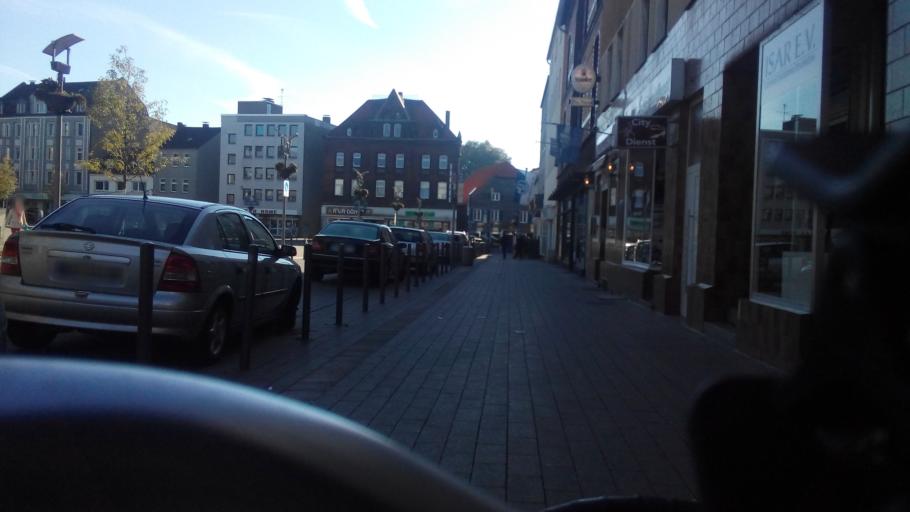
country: DE
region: North Rhine-Westphalia
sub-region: Regierungsbezirk Munster
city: Gelsenkirchen
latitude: 51.5126
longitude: 7.0956
